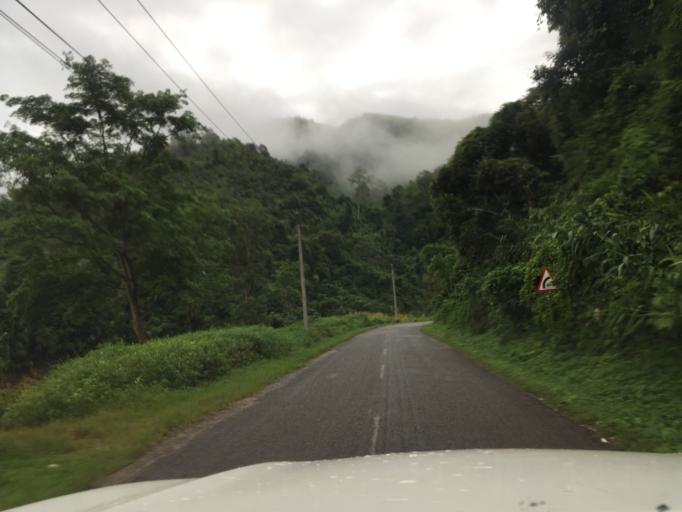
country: LA
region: Oudomxai
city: Muang La
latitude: 20.9402
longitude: 102.2079
